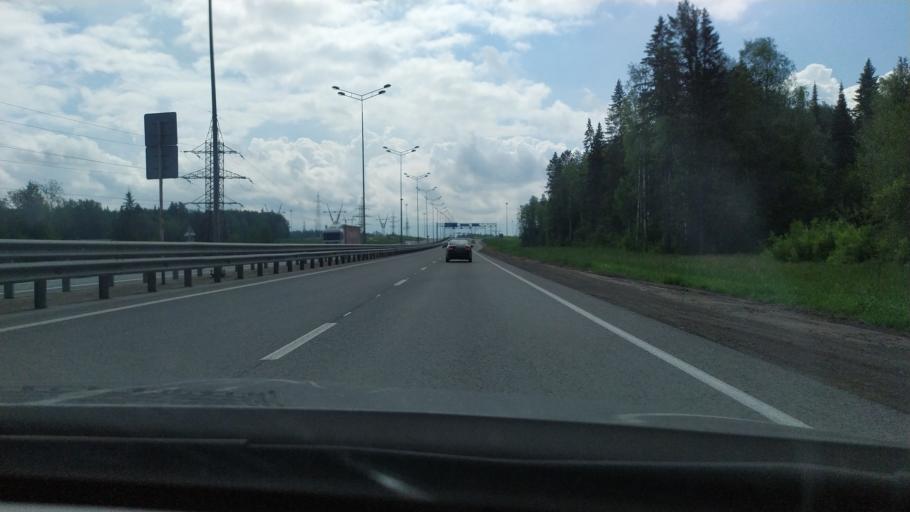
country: RU
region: Perm
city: Novyye Lyady
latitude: 58.0524
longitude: 56.4286
